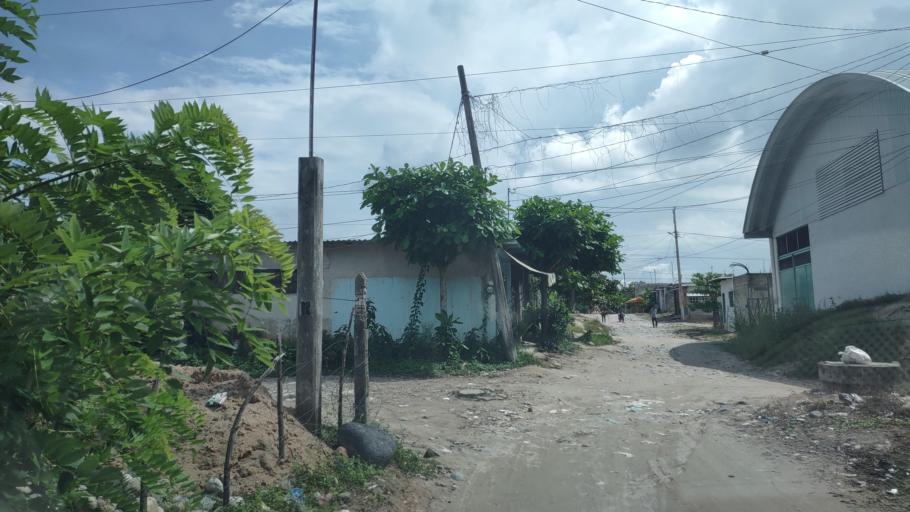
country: MX
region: Veracruz
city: Martinez de la Torre
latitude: 20.0765
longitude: -97.0798
